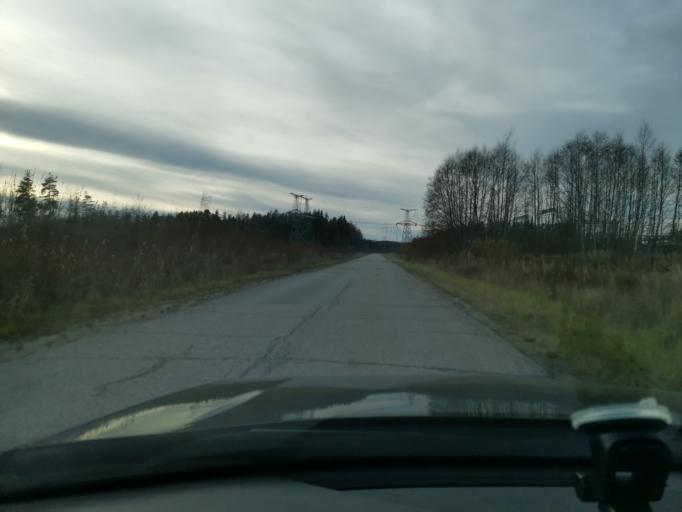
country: EE
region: Ida-Virumaa
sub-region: Sillamaee linn
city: Sillamae
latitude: 59.2680
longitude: 27.9075
